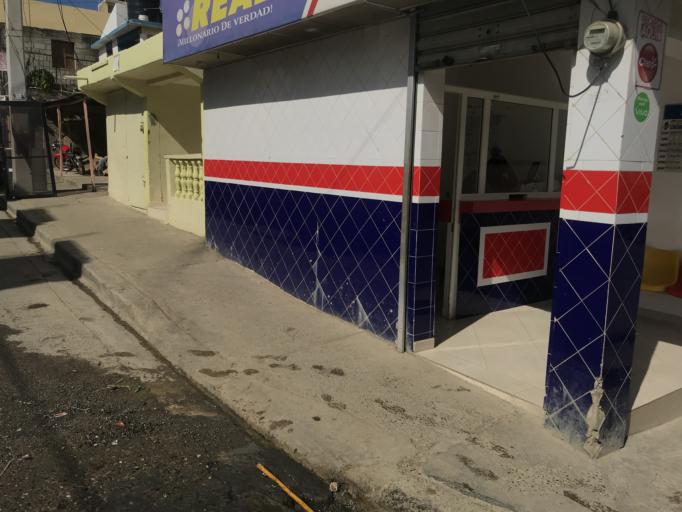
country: DO
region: Santiago
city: Santiago de los Caballeros
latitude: 19.4811
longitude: -70.7470
